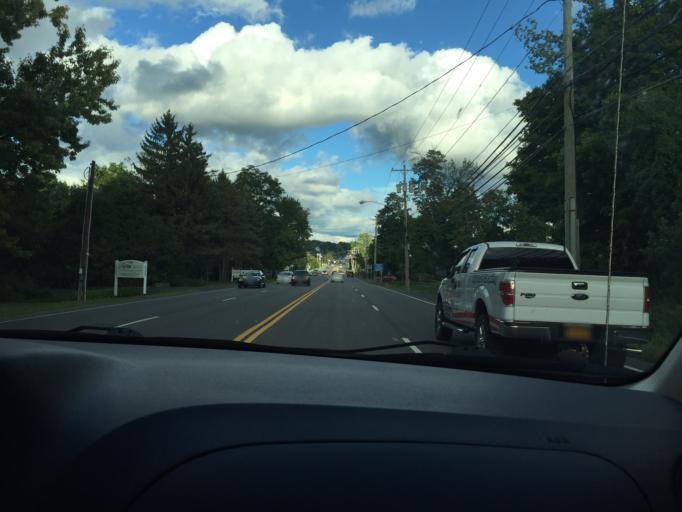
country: US
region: New York
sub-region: Onondaga County
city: Fayetteville
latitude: 43.0289
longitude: -76.0255
